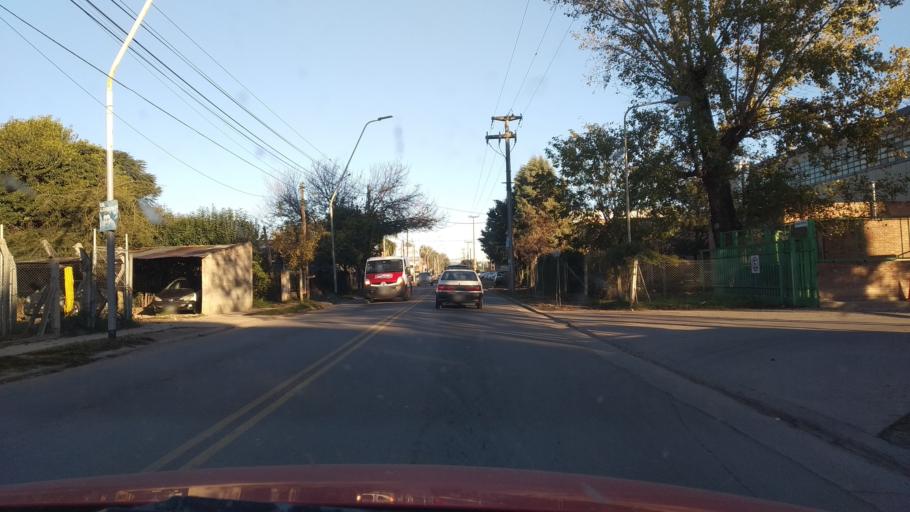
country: AR
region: Cordoba
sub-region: Departamento de Capital
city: Cordoba
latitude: -31.3432
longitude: -64.2093
